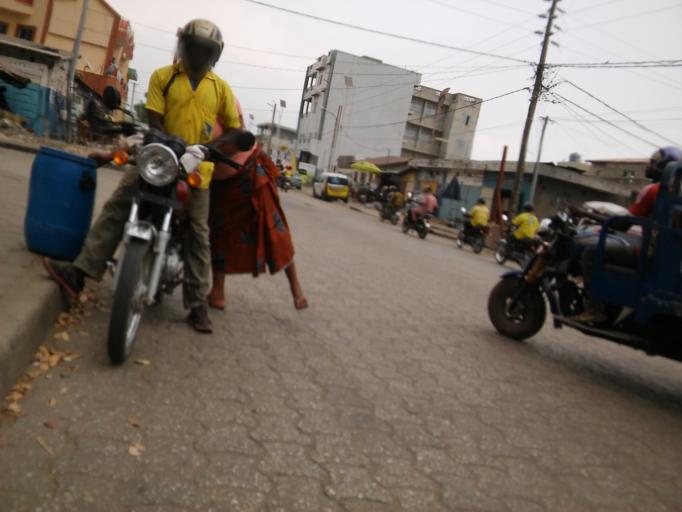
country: BJ
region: Littoral
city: Cotonou
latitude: 6.3846
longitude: 2.4059
